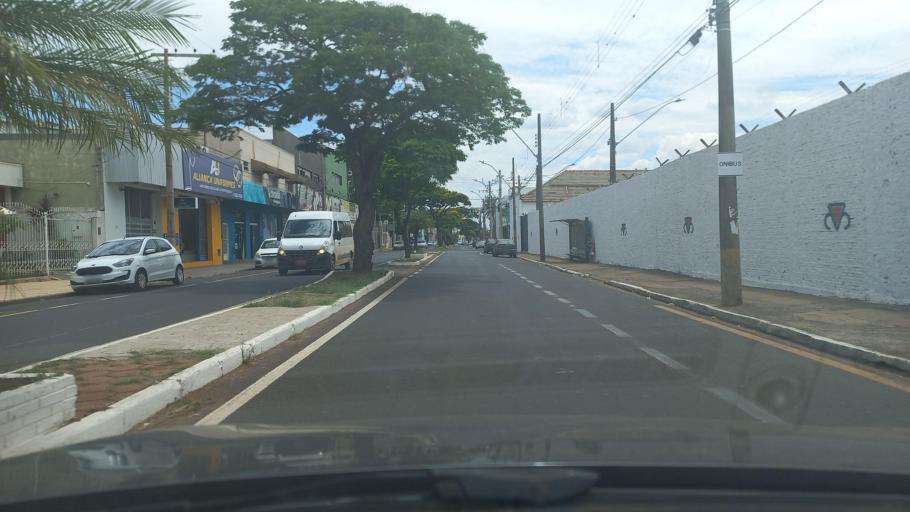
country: BR
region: Minas Gerais
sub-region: Uberaba
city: Uberaba
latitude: -19.7705
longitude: -47.9492
